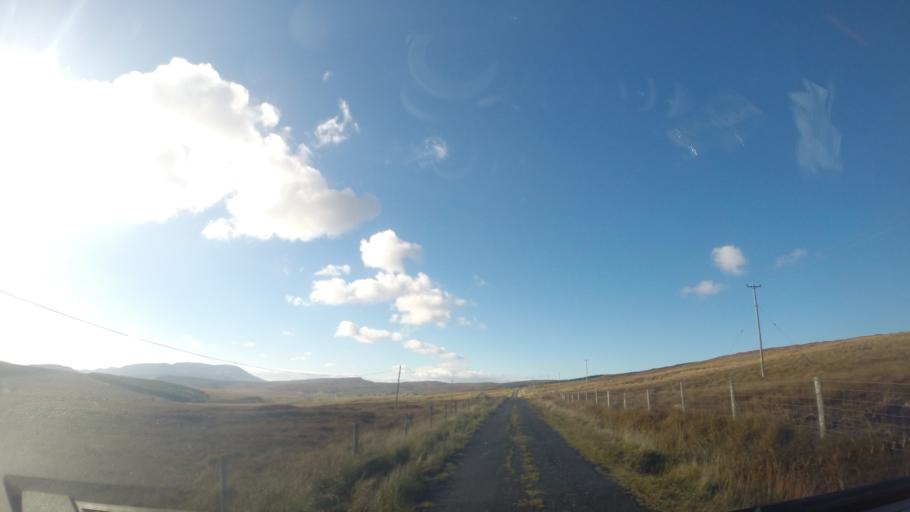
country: IE
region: Ulster
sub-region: County Donegal
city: Killybegs
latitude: 54.7218
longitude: -8.5746
